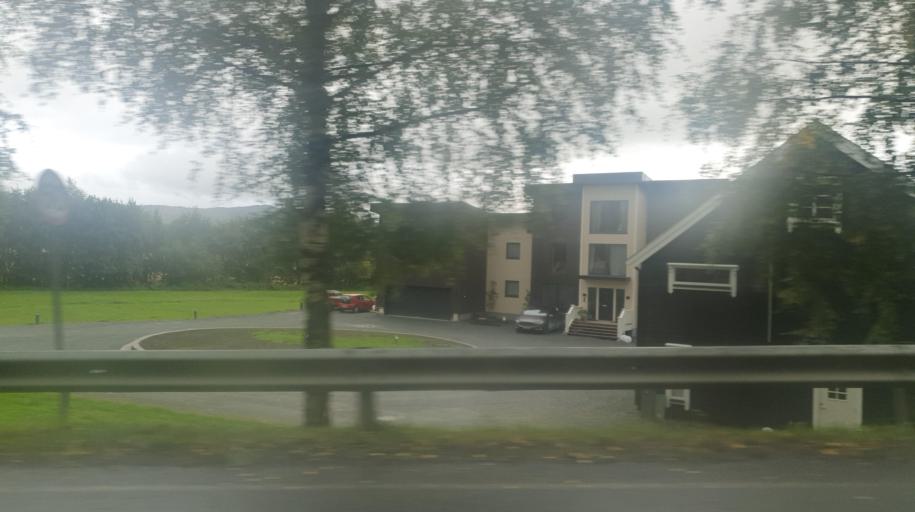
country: NO
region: Nord-Trondelag
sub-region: Verdal
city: Verdal
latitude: 63.7962
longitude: 11.5273
